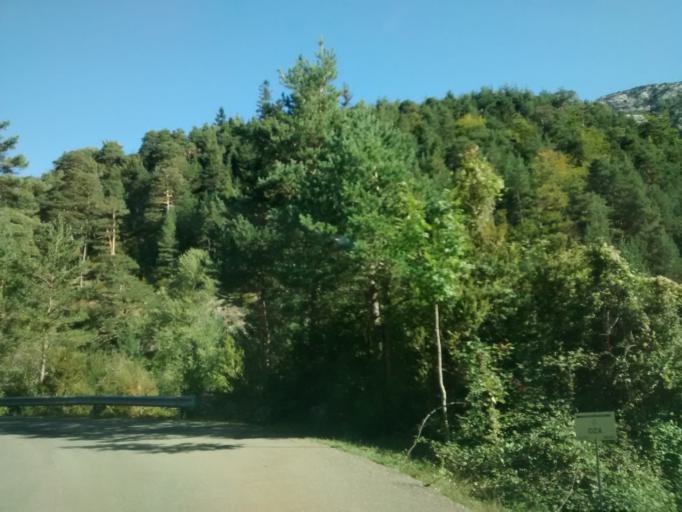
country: ES
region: Aragon
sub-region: Provincia de Huesca
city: Aragues del Puerto
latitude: 42.8128
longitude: -0.7114
